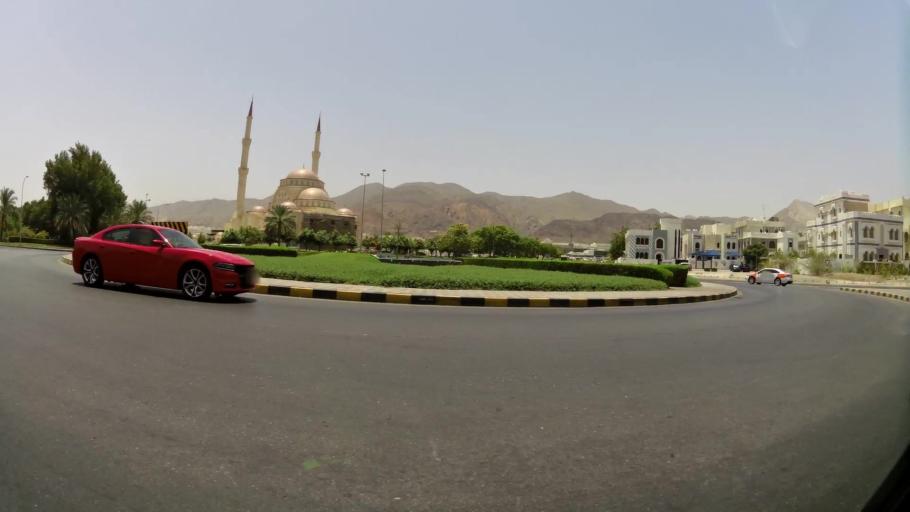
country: OM
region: Muhafazat Masqat
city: Bawshar
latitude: 23.5845
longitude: 58.4293
